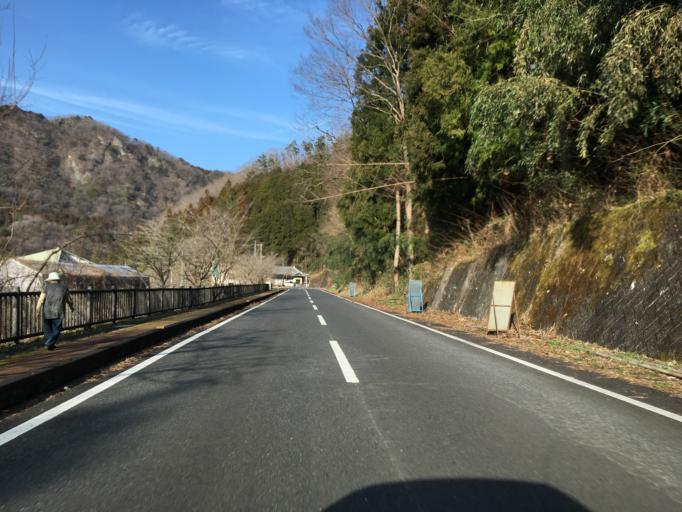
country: JP
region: Ibaraki
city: Daigo
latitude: 36.7594
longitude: 140.3972
